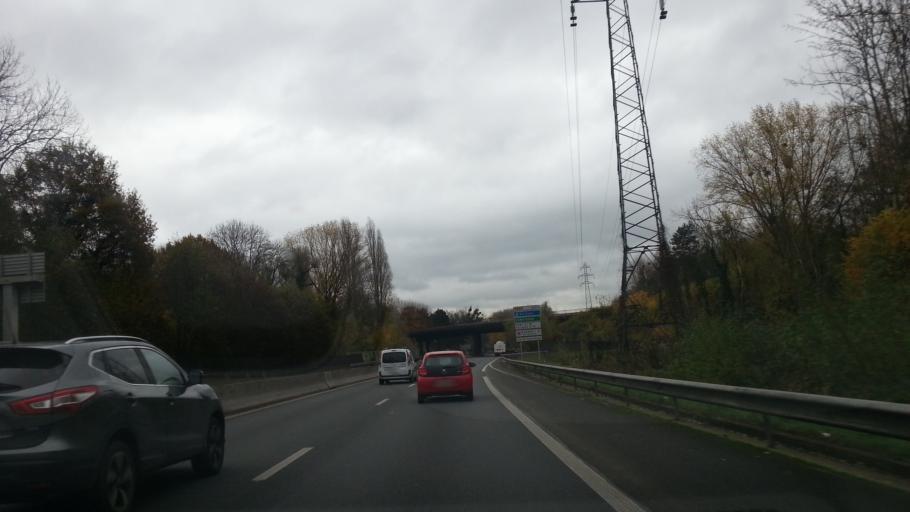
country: FR
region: Picardie
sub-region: Departement de l'Oise
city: Monchy-Saint-Eloi
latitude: 49.2875
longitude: 2.4668
